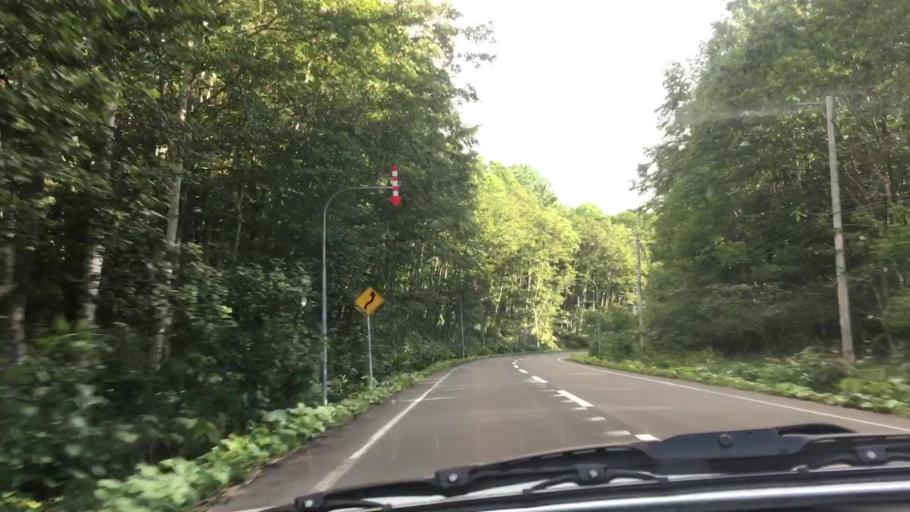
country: JP
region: Hokkaido
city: Shimo-furano
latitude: 43.0947
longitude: 142.6861
